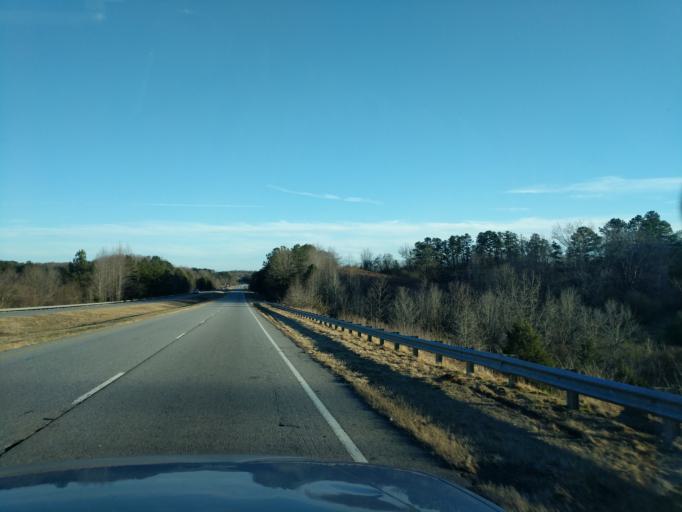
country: US
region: Georgia
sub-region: Stephens County
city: Toccoa
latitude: 34.5505
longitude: -83.3709
